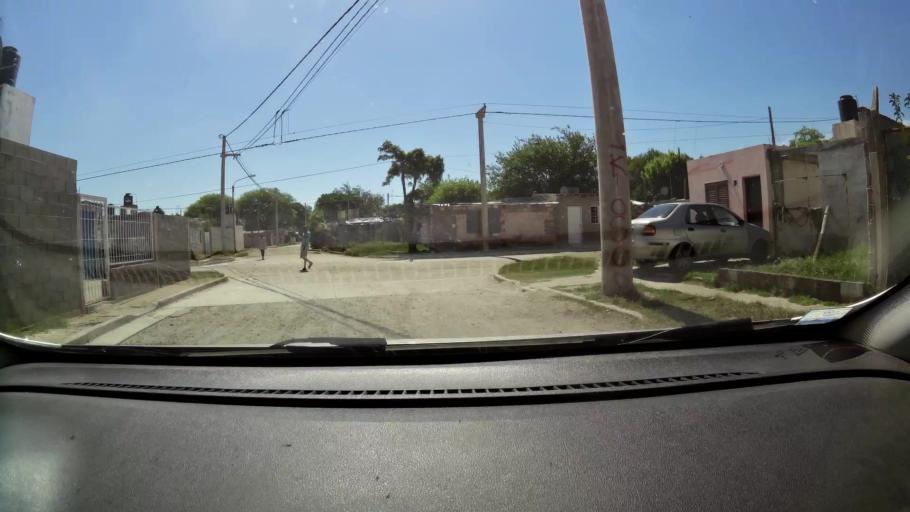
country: AR
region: Cordoba
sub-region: Departamento de Capital
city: Cordoba
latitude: -31.3704
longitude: -64.1575
